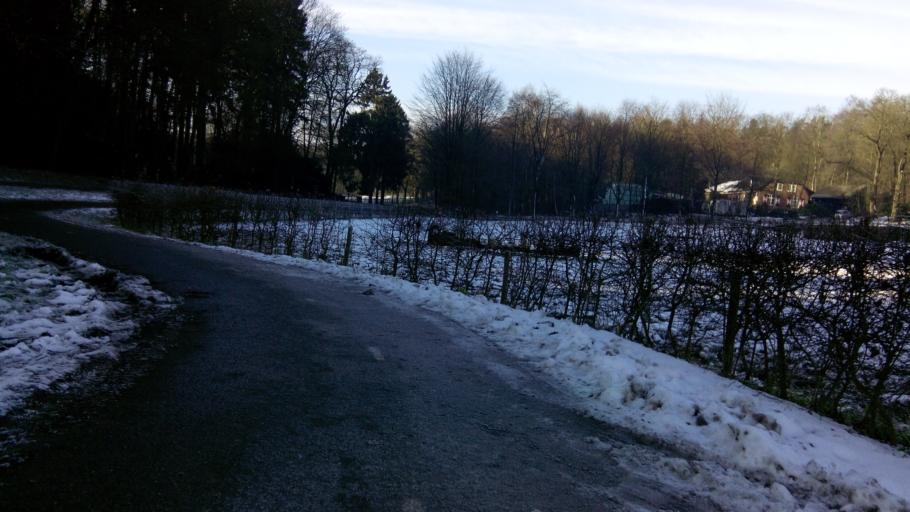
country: NL
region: Gelderland
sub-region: Gemeente Groesbeek
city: Berg en Dal
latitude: 51.8140
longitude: 5.9029
